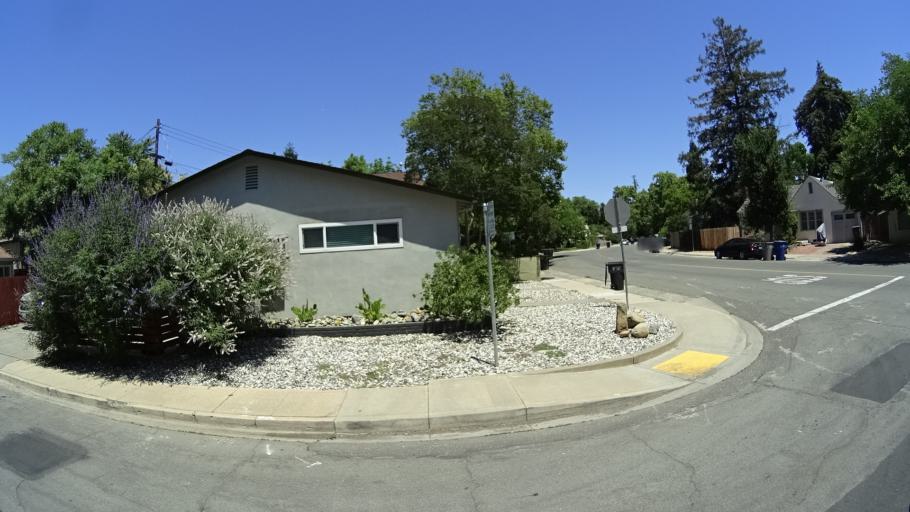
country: US
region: California
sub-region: Sacramento County
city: Sacramento
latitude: 38.5541
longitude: -121.4647
